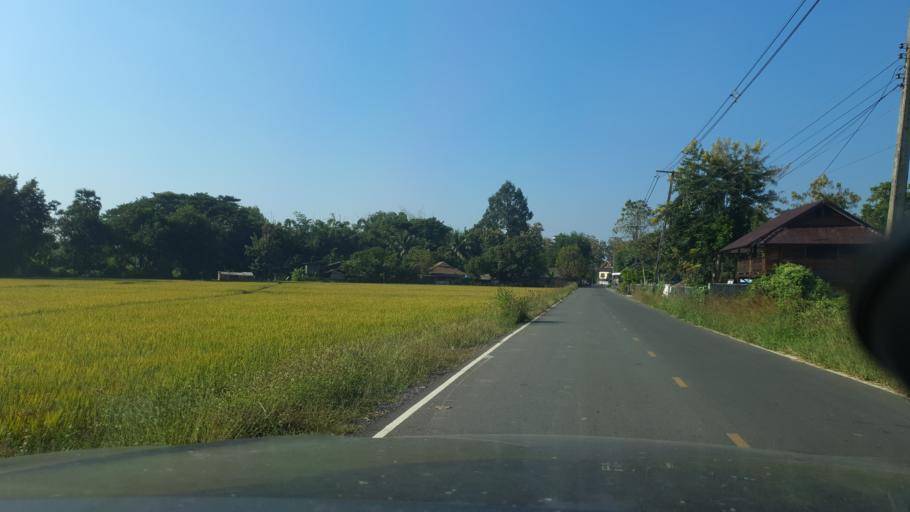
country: TH
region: Chiang Mai
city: San Kamphaeng
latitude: 18.7528
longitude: 99.1497
